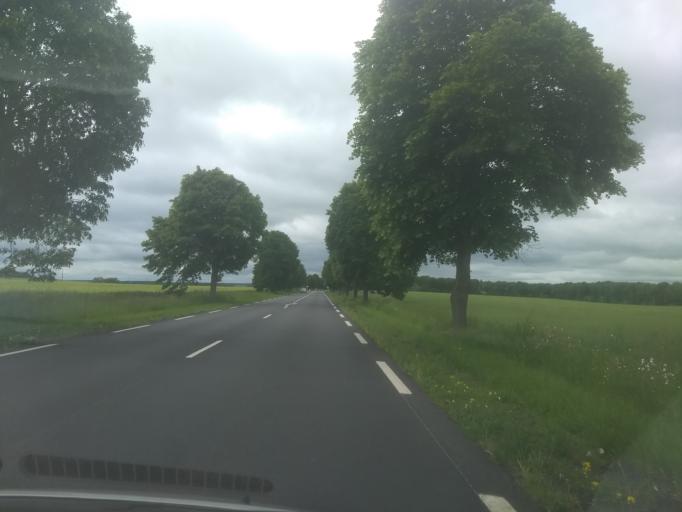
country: FR
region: Centre
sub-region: Departement d'Eure-et-Loir
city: Treon
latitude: 48.6536
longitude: 1.2965
